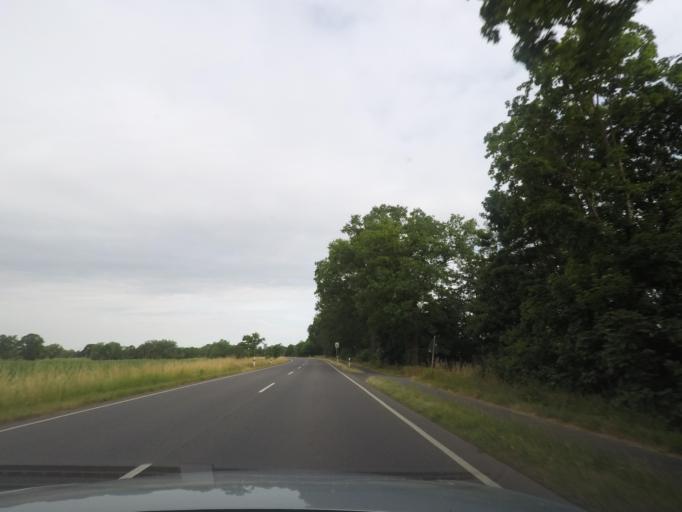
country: DE
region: Lower Saxony
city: Meinersen
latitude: 52.4439
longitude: 10.3205
